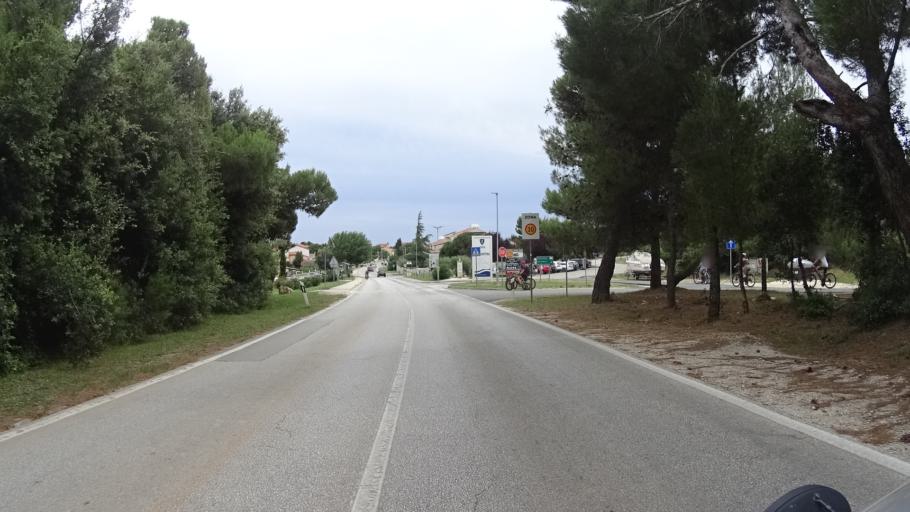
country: HR
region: Istarska
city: Medulin
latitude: 44.8064
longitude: 13.9091
